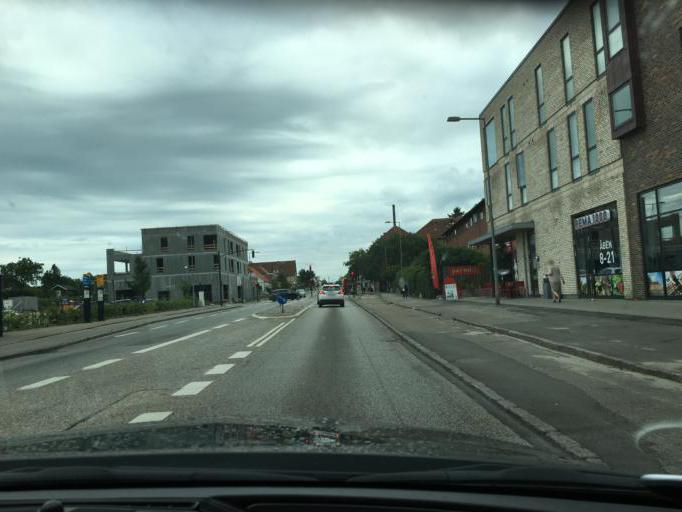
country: DK
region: Capital Region
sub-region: Horsholm Kommune
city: Horsholm
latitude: 55.8874
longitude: 12.4971
